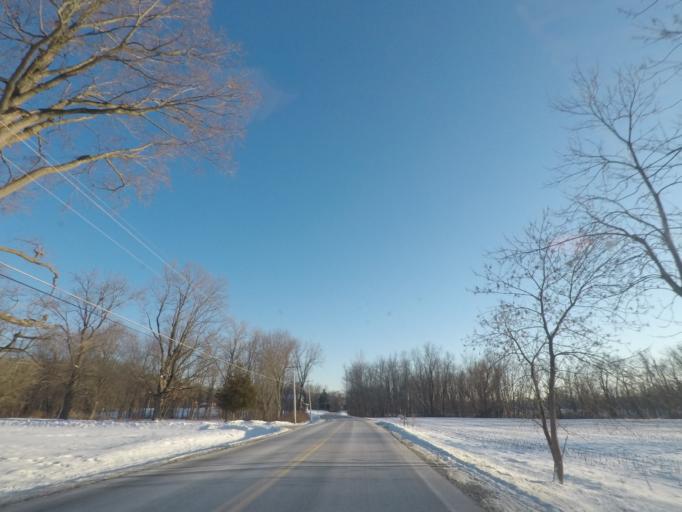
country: US
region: New York
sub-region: Saratoga County
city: Waterford
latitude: 42.8406
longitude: -73.6671
